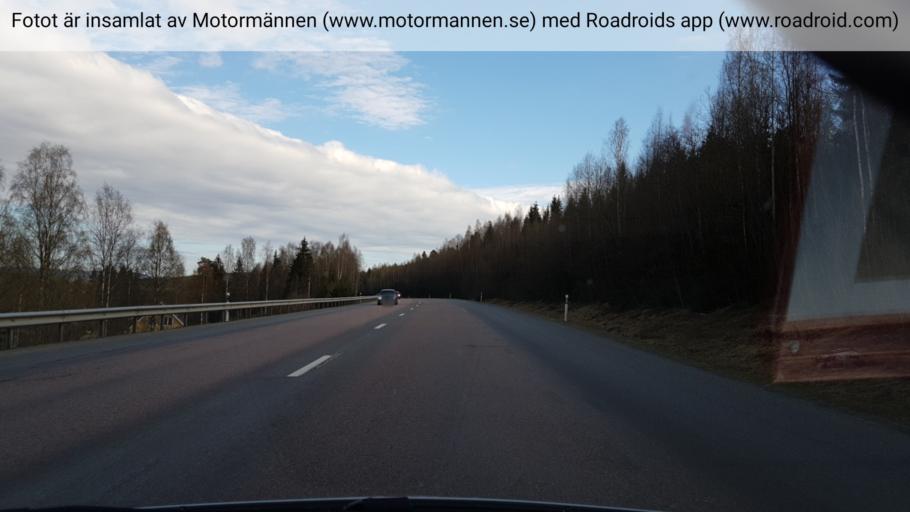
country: SE
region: Vaesternorrland
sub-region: Kramfors Kommun
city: Bollstabruk
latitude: 62.9699
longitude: 17.7242
